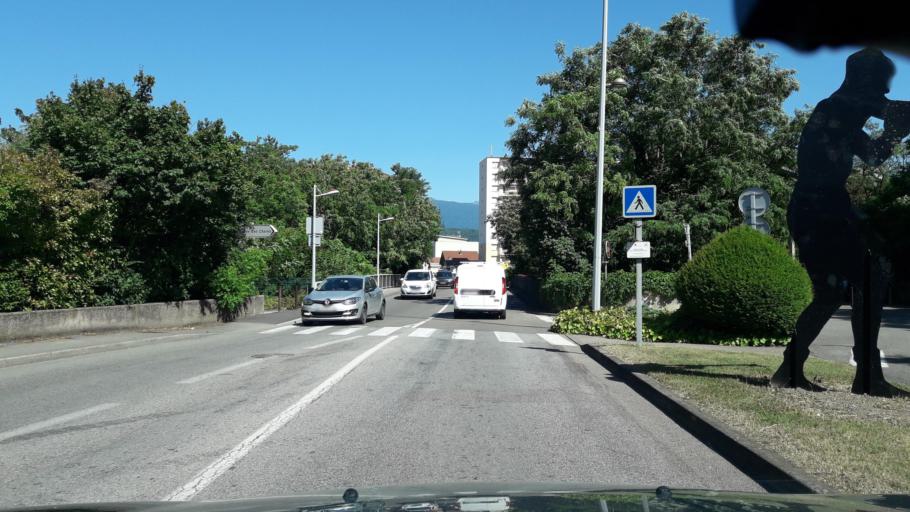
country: FR
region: Rhone-Alpes
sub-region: Departement de l'Isere
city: Seyssins
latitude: 45.1495
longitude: 5.7000
